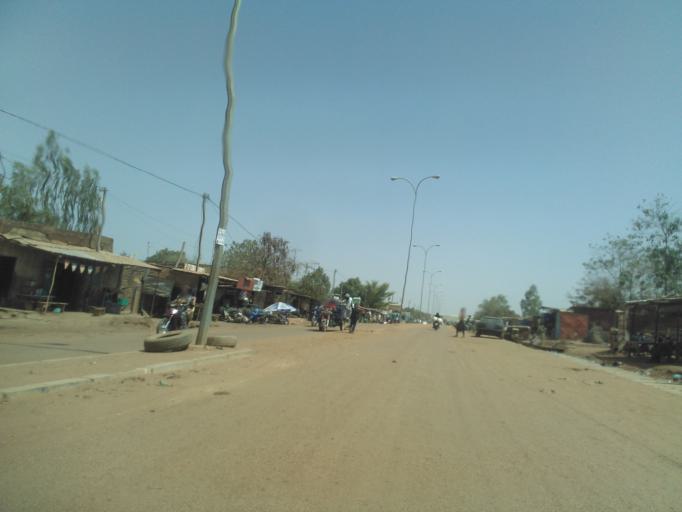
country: BF
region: Centre
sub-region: Kadiogo Province
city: Ouagadougou
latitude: 12.3896
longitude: -1.5631
